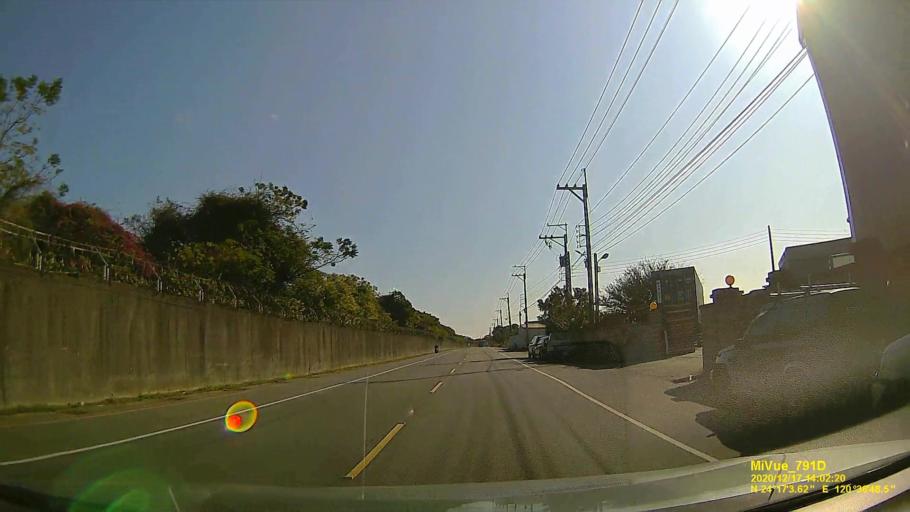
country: TW
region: Taiwan
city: Fengyuan
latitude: 24.2843
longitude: 120.6135
